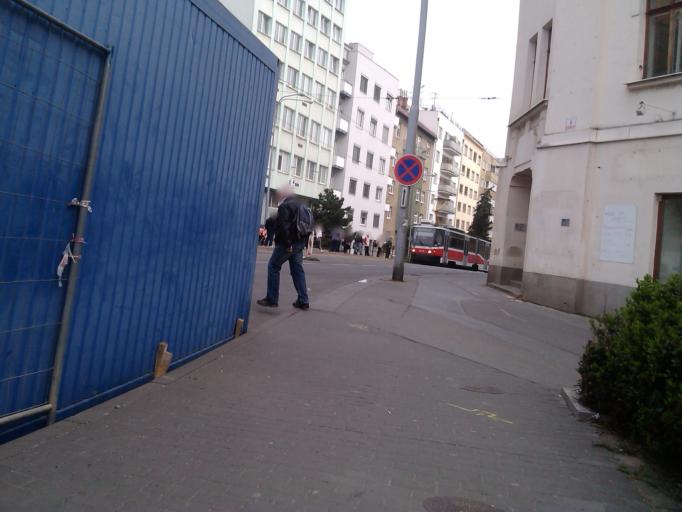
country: CZ
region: South Moravian
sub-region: Mesto Brno
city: Brno
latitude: 49.2028
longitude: 16.6187
